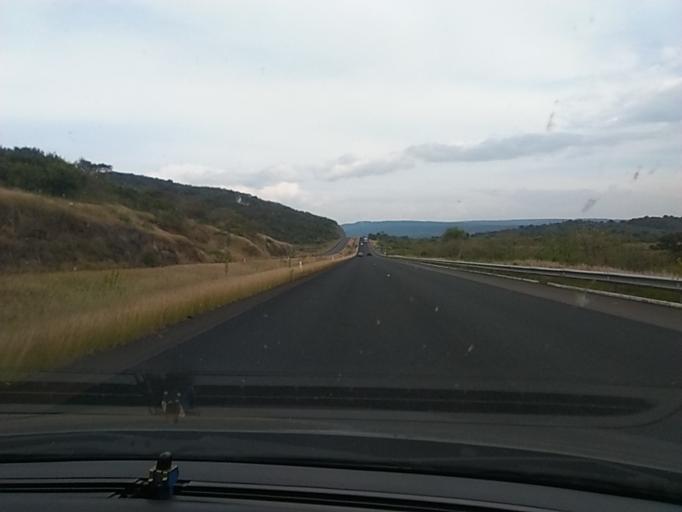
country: MX
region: Mexico
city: Huaniqueo de Morales
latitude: 19.8833
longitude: -101.4246
